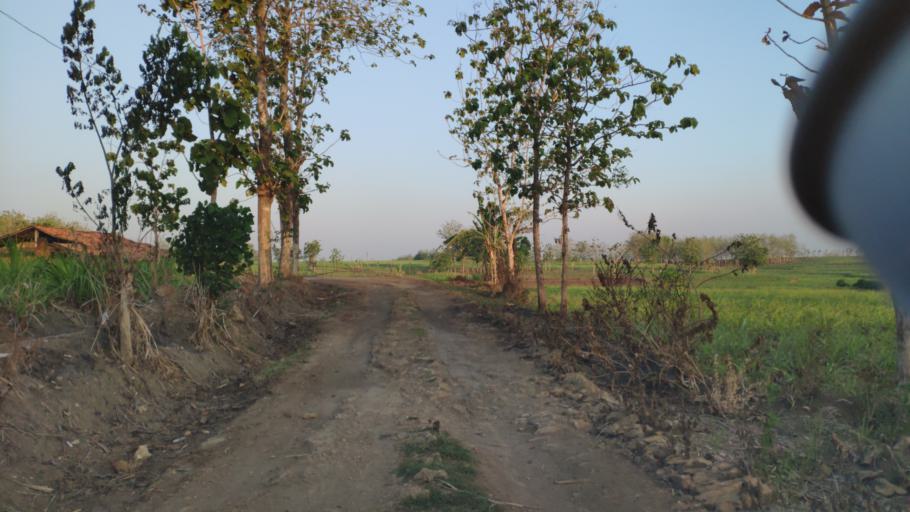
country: ID
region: Central Java
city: Jepang
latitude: -7.0287
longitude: 111.2324
